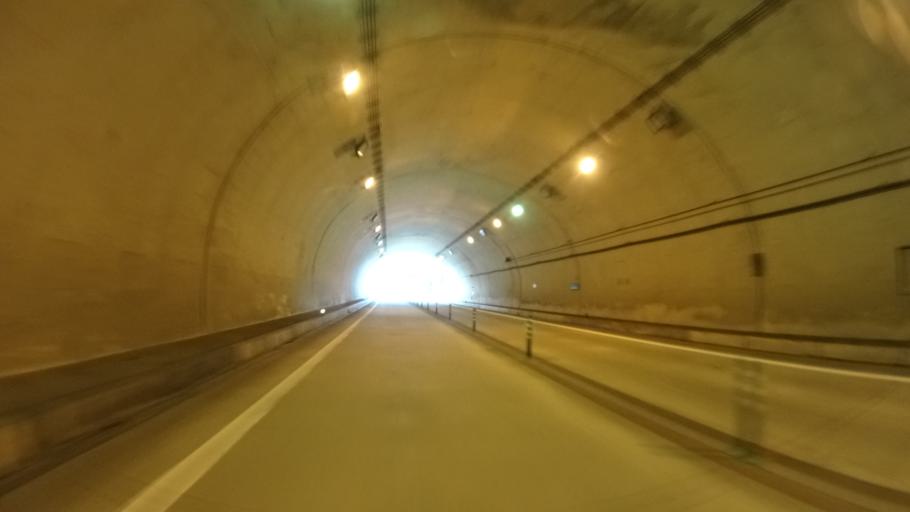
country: JP
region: Toyama
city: Himi
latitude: 36.8901
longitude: 136.9810
